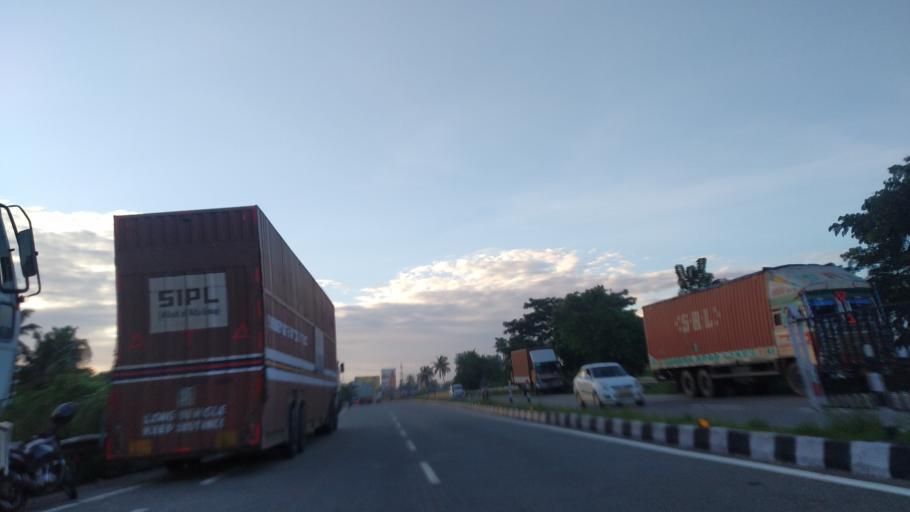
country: IN
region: Kerala
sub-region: Ernakulam
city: Elur
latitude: 10.0653
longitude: 76.3253
